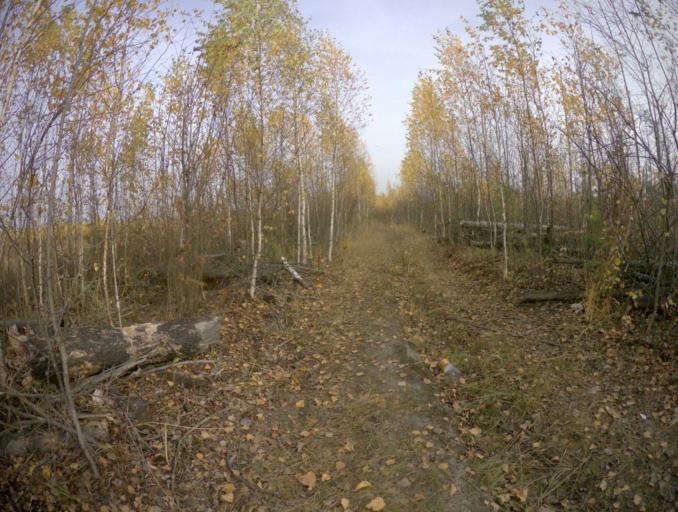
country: RU
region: Vladimir
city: Sobinka
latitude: 55.9724
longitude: 40.0626
